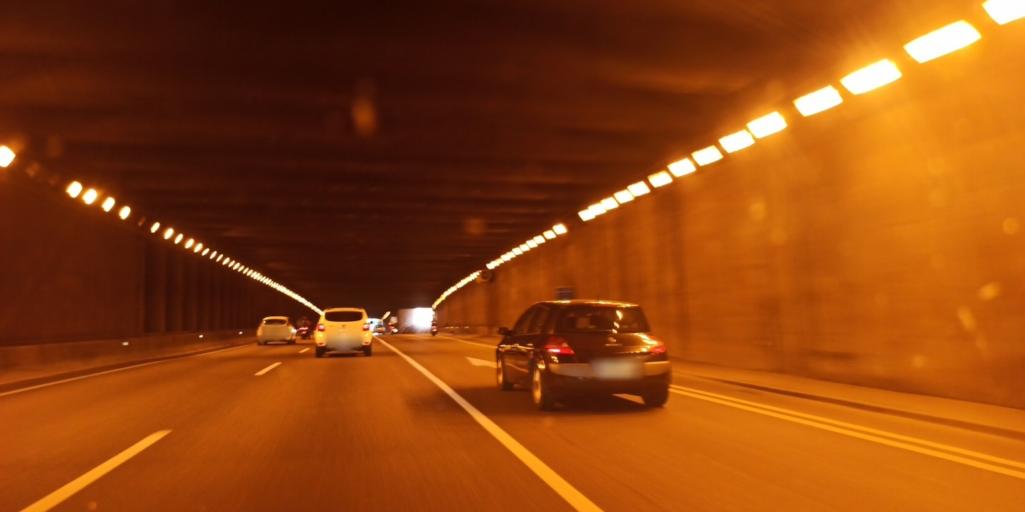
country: ES
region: Catalonia
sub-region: Provincia de Barcelona
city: Esplugues de Llobregat
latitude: 41.3661
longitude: 2.0901
